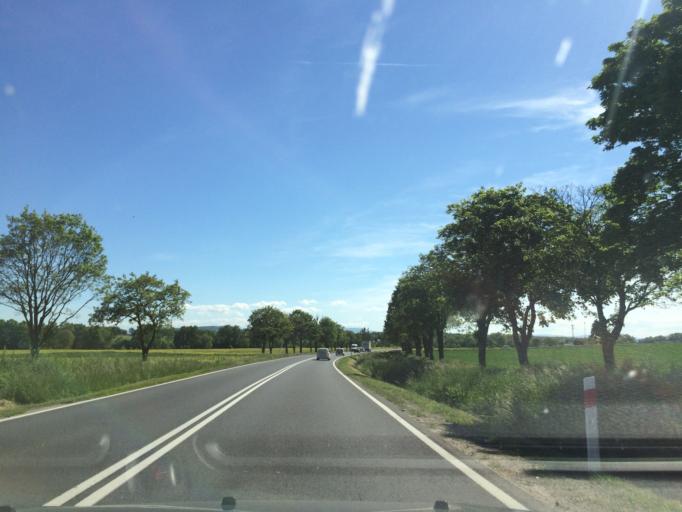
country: PL
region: Lower Silesian Voivodeship
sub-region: Powiat wroclawski
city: Sobotka
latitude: 50.9186
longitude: 16.6768
